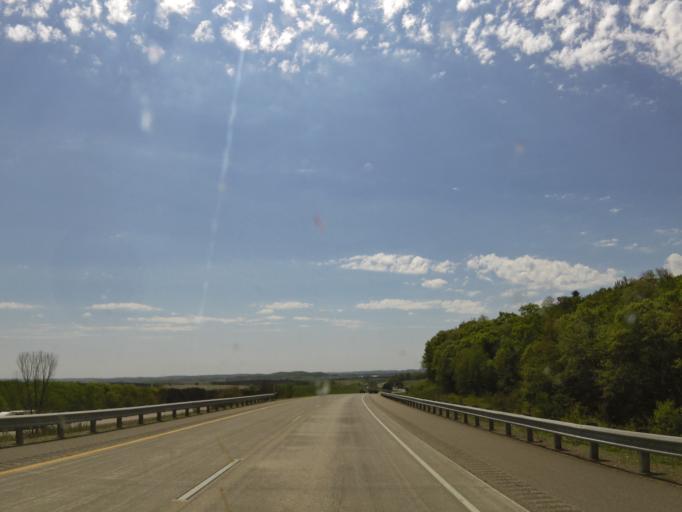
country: US
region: Wisconsin
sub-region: Trempealeau County
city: Osseo
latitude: 44.6078
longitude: -91.2301
